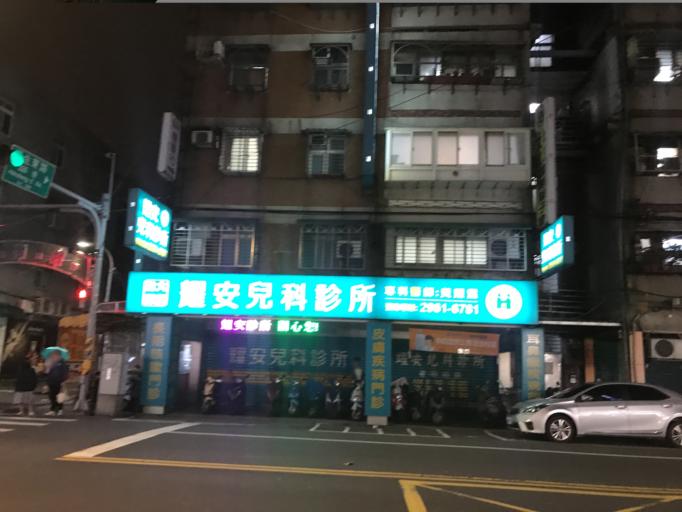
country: TW
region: Taipei
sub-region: Taipei
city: Banqiao
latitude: 25.0083
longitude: 121.4718
